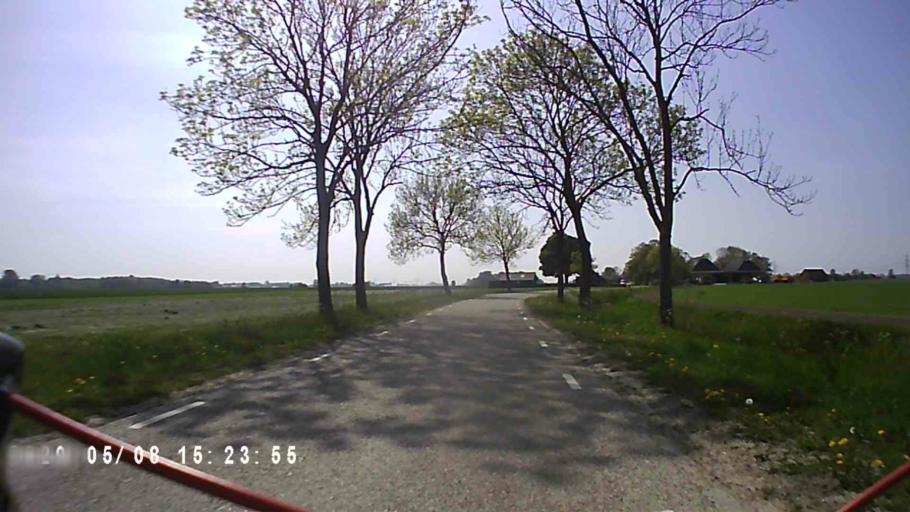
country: NL
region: Groningen
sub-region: Gemeente Appingedam
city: Appingedam
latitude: 53.3582
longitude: 6.7653
